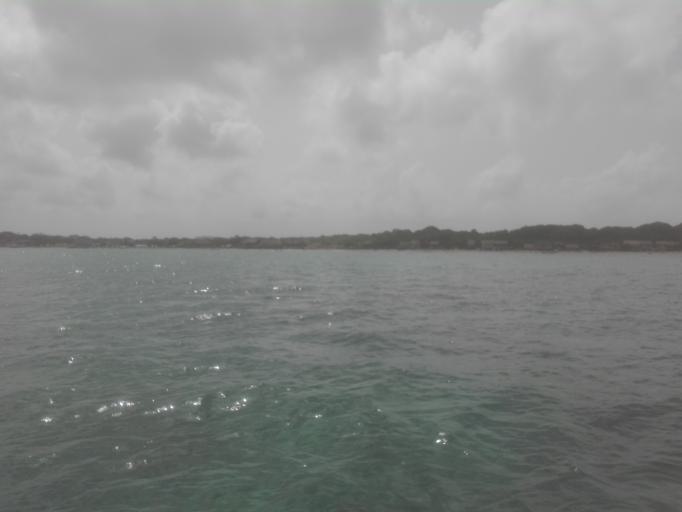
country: CO
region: Bolivar
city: Turbana
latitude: 10.2272
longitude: -75.6104
